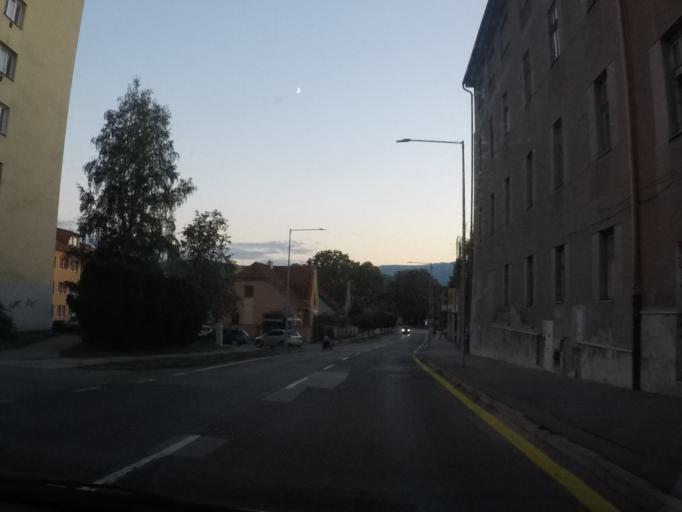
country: SK
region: Kosicky
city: Spisska Nova Ves
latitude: 48.9430
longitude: 20.5665
